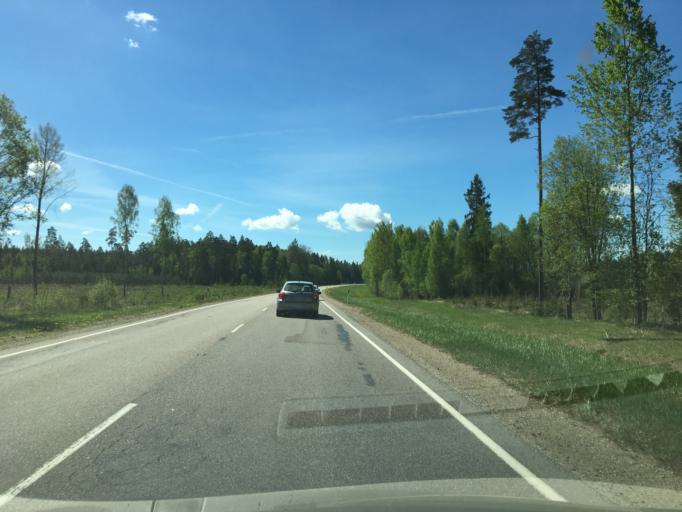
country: EE
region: Valgamaa
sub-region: Valga linn
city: Valga
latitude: 57.8873
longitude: 26.1653
